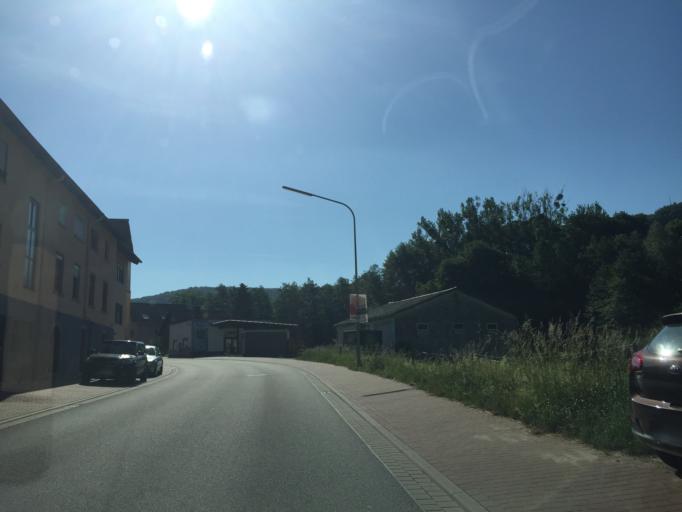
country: DE
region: Hesse
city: Unter-Abtsteinach
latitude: 49.5269
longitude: 8.7527
